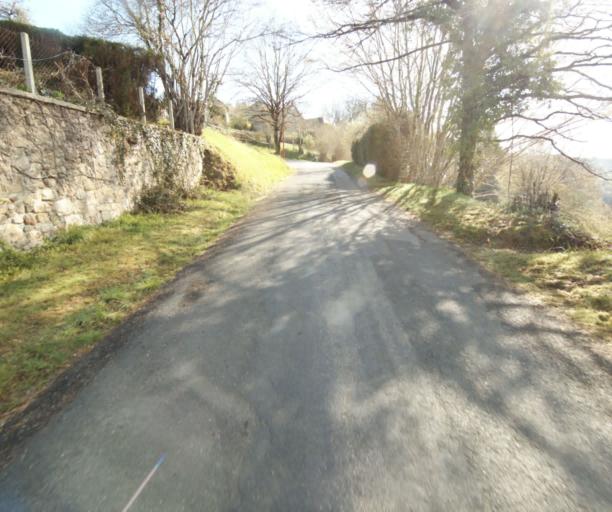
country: FR
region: Limousin
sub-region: Departement de la Correze
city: Laguenne
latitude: 45.2563
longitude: 1.8334
